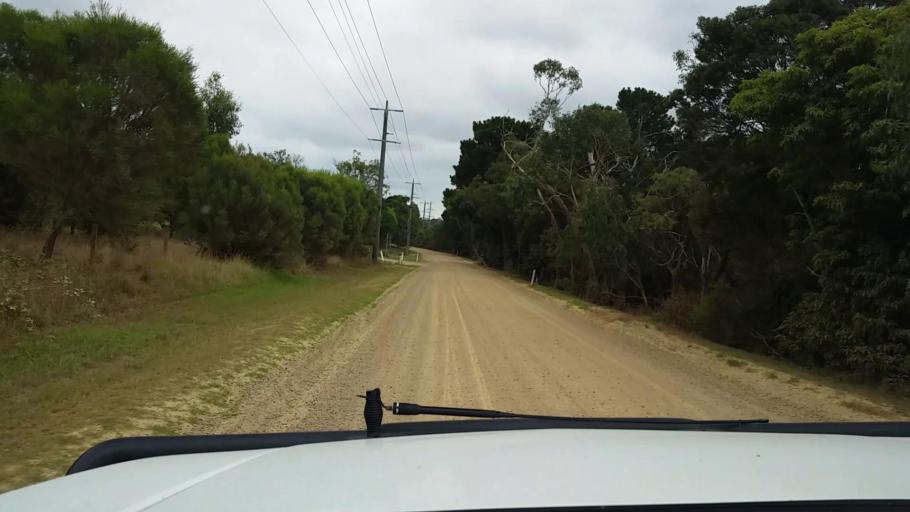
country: AU
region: Victoria
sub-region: Mornington Peninsula
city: Moorooduc
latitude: -38.2784
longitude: 145.1065
